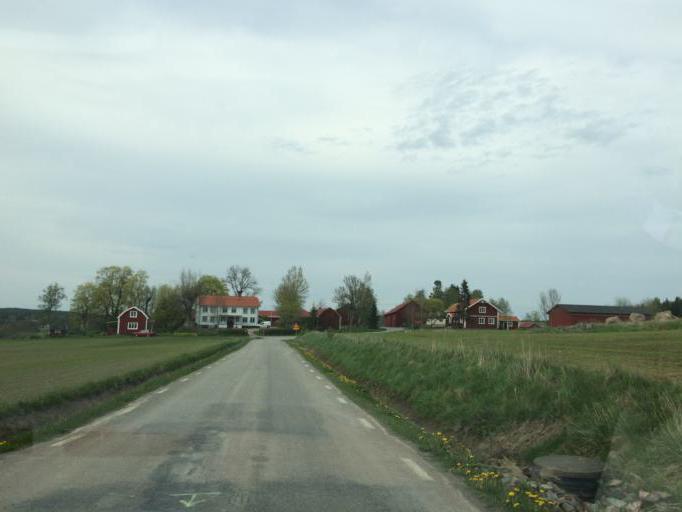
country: SE
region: Vaestmanland
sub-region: Kopings Kommun
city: Koping
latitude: 59.6116
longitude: 16.0295
